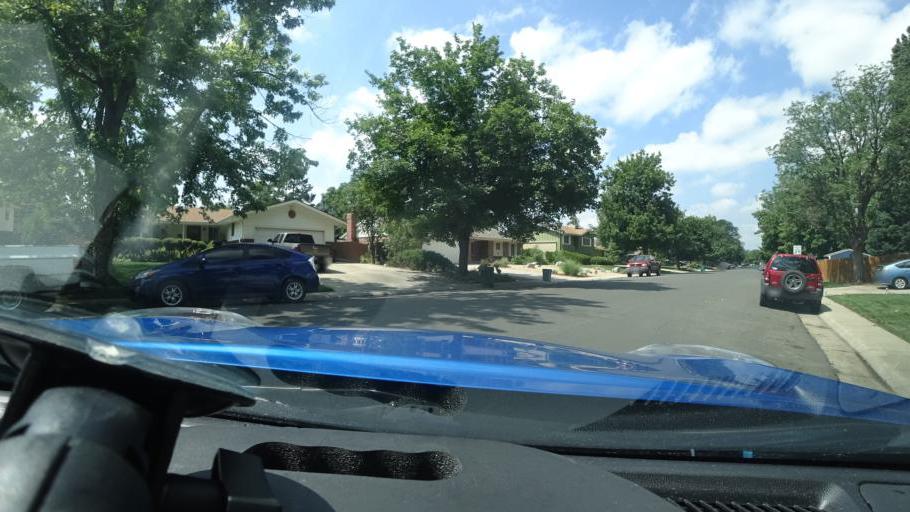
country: US
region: Colorado
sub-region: Adams County
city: Aurora
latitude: 39.7189
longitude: -104.8540
